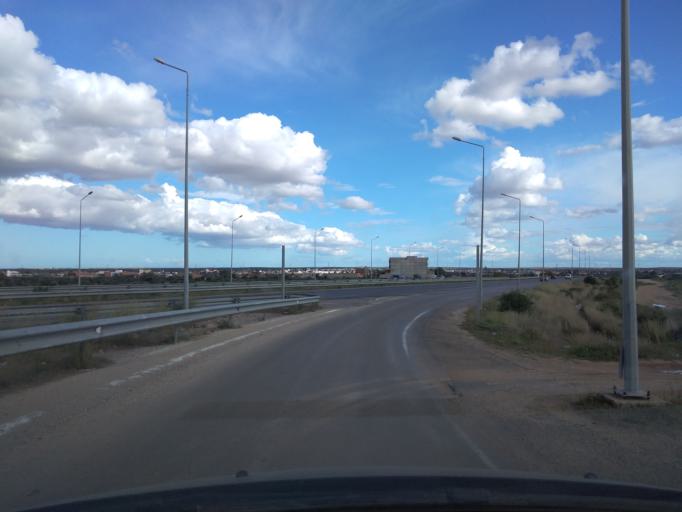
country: TN
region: Susah
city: Masakin
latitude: 35.7113
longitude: 10.5583
